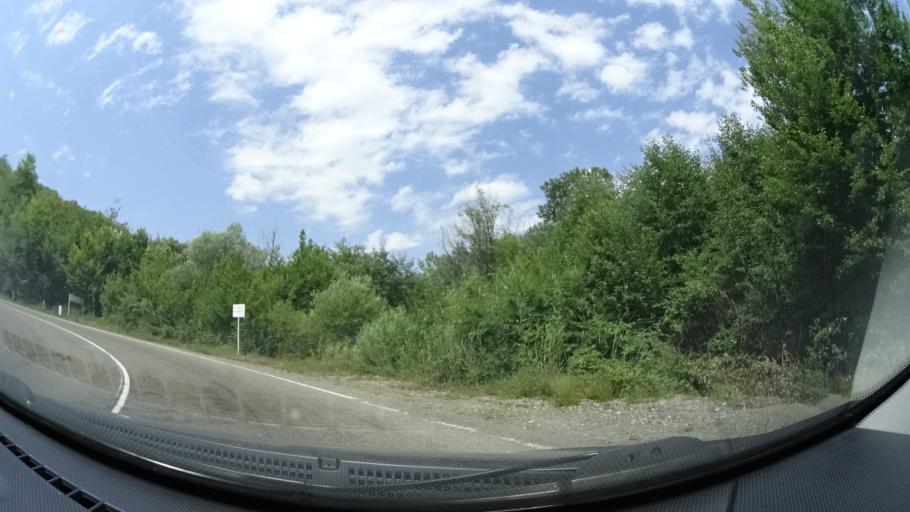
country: GE
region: Kakheti
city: Sagarejo
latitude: 41.8686
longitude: 45.3475
